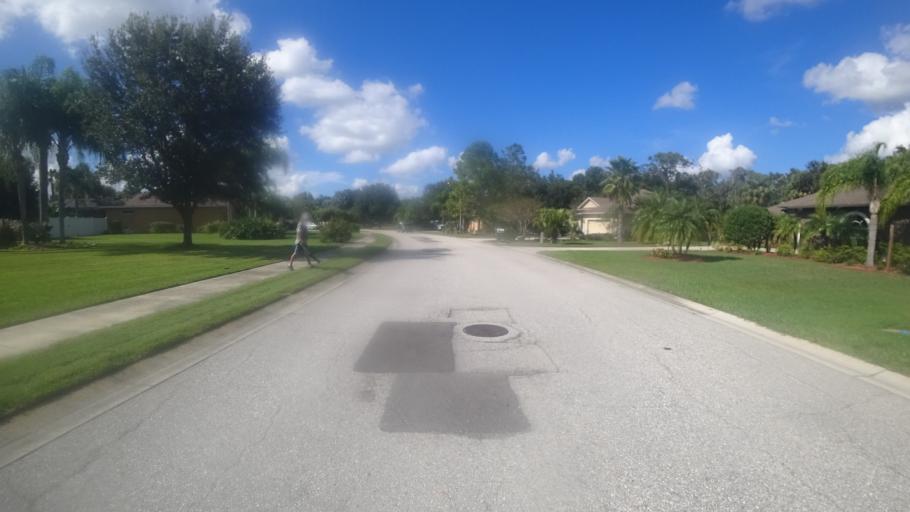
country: US
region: Florida
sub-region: Manatee County
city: Ellenton
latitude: 27.5012
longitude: -82.3978
